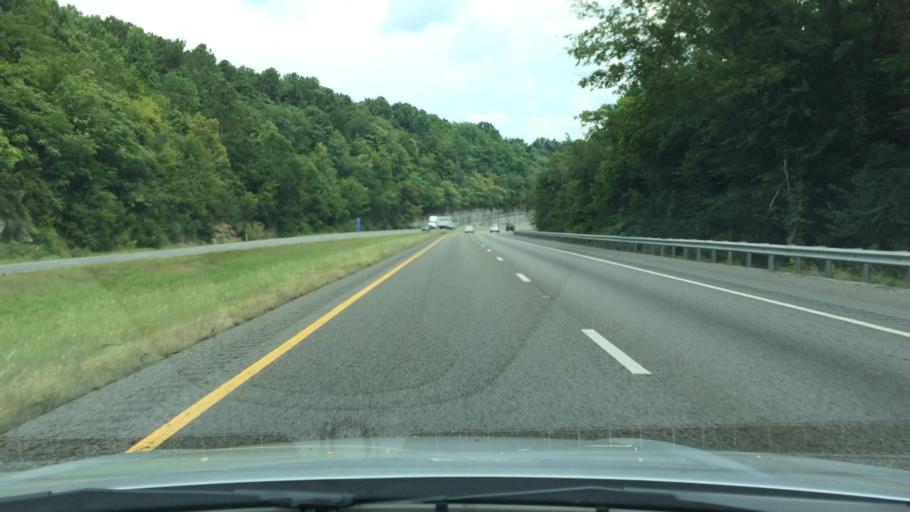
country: US
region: Tennessee
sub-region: Marshall County
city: Cornersville
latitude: 35.4013
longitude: -86.8805
